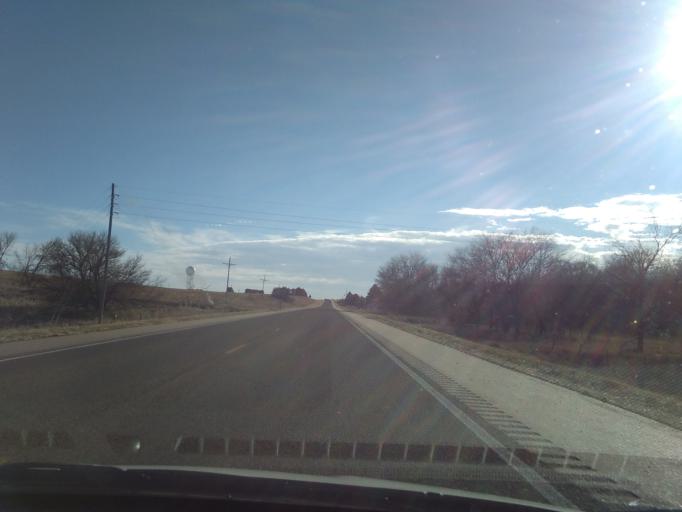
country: US
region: Nebraska
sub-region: Webster County
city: Red Cloud
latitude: 40.3282
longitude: -98.4439
